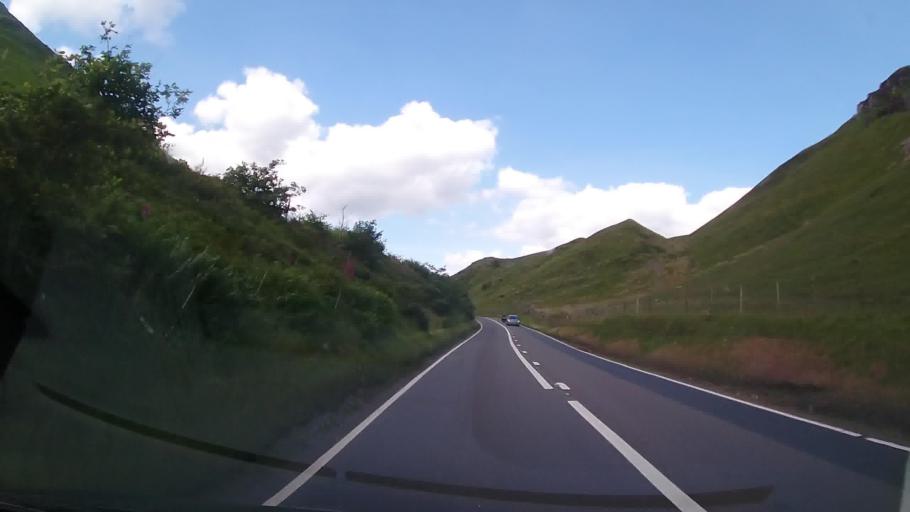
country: GB
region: Wales
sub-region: Gwynedd
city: Dolgellau
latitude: 52.7069
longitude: -3.8440
